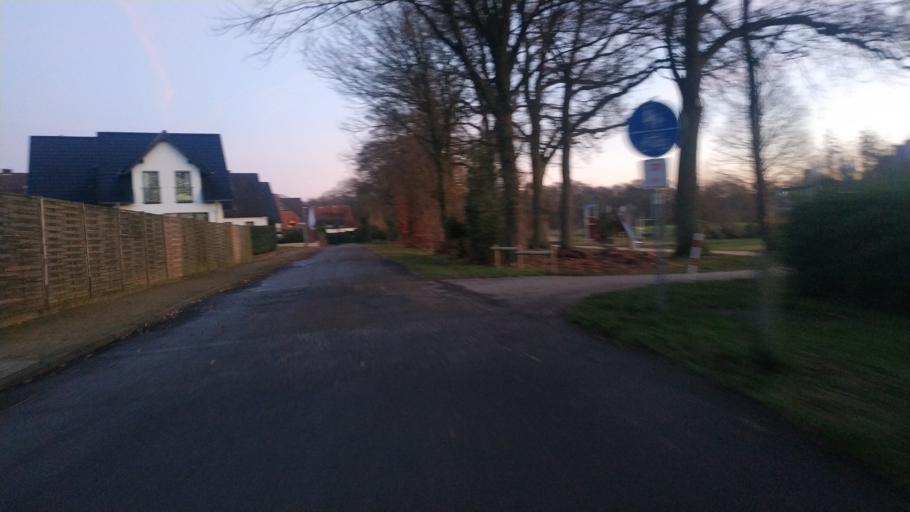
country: DE
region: North Rhine-Westphalia
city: Ibbenburen
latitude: 52.2694
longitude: 7.7018
